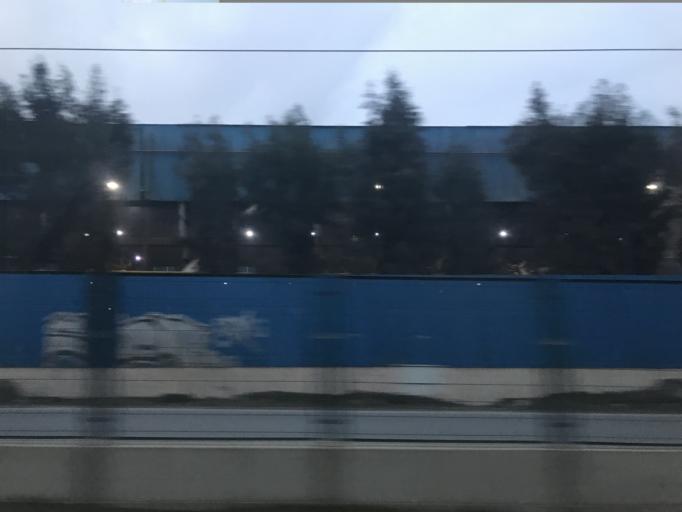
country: TR
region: Kocaeli
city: Darica
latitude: 40.8025
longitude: 29.3747
